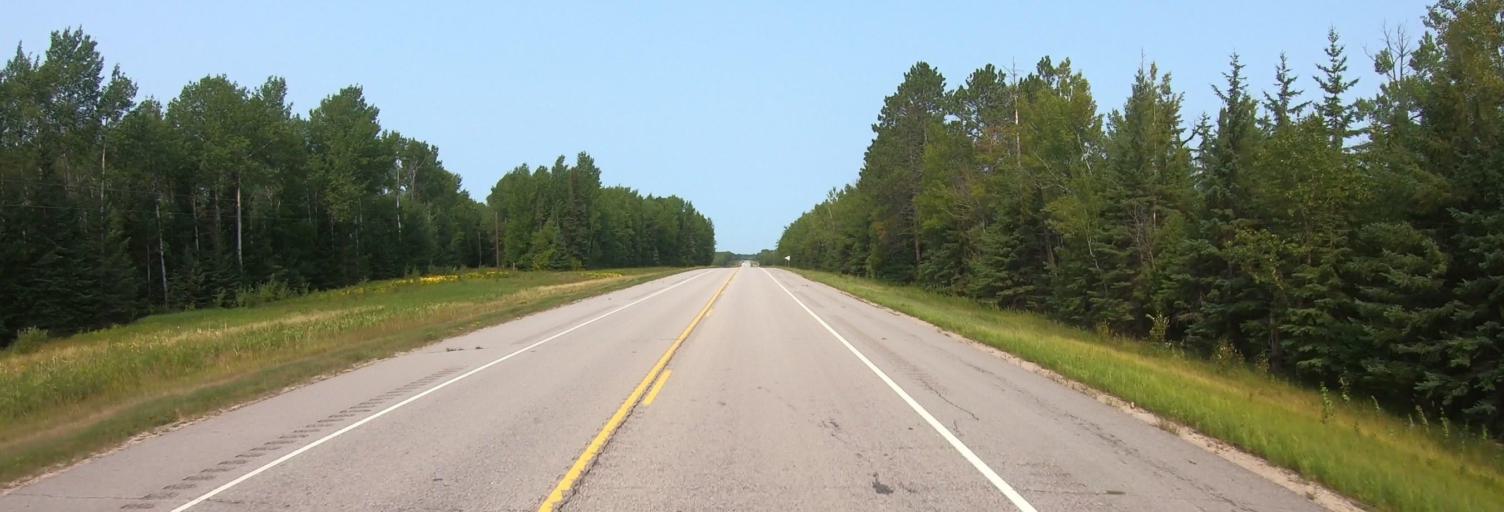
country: CA
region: Ontario
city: Fort Frances
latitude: 48.3781
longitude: -92.9835
